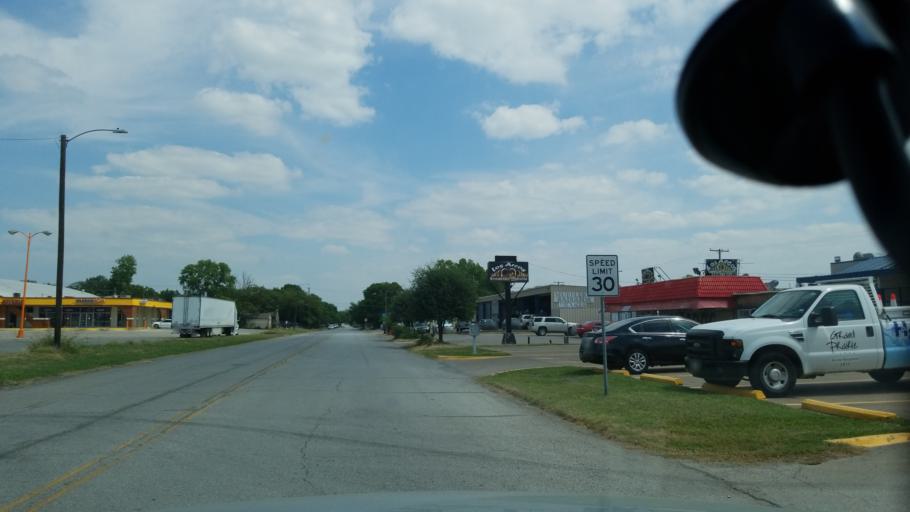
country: US
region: Texas
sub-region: Dallas County
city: Grand Prairie
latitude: 32.7493
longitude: -96.9780
